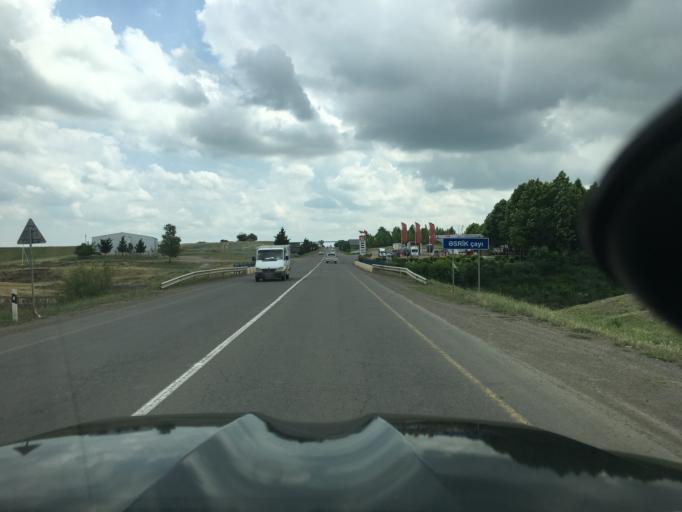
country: AZ
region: Tovuz
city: Tovuz
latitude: 40.9755
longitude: 45.6739
